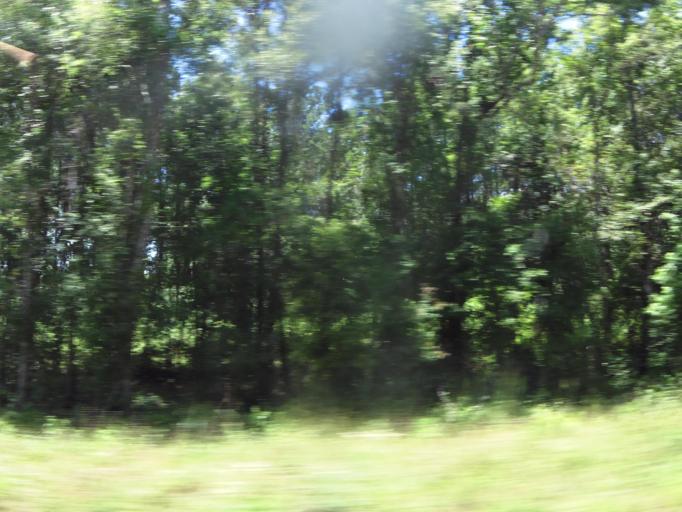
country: US
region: Florida
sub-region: Bradford County
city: Starke
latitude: 30.0300
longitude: -82.1905
